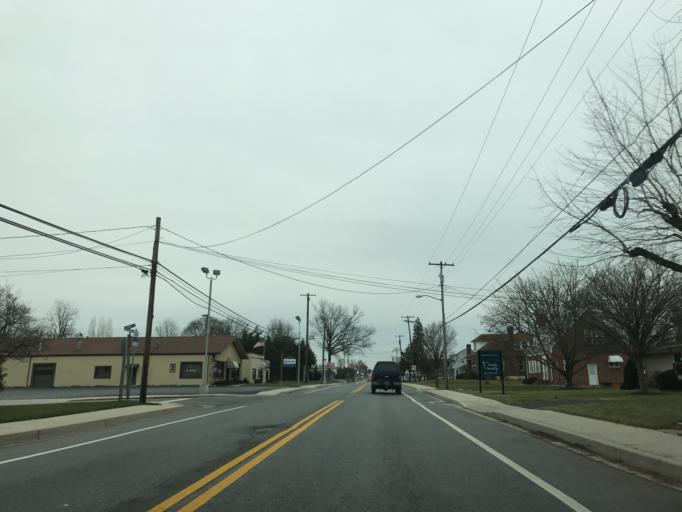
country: US
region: Maryland
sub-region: Carroll County
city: Taneytown
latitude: 39.6523
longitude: -77.1638
